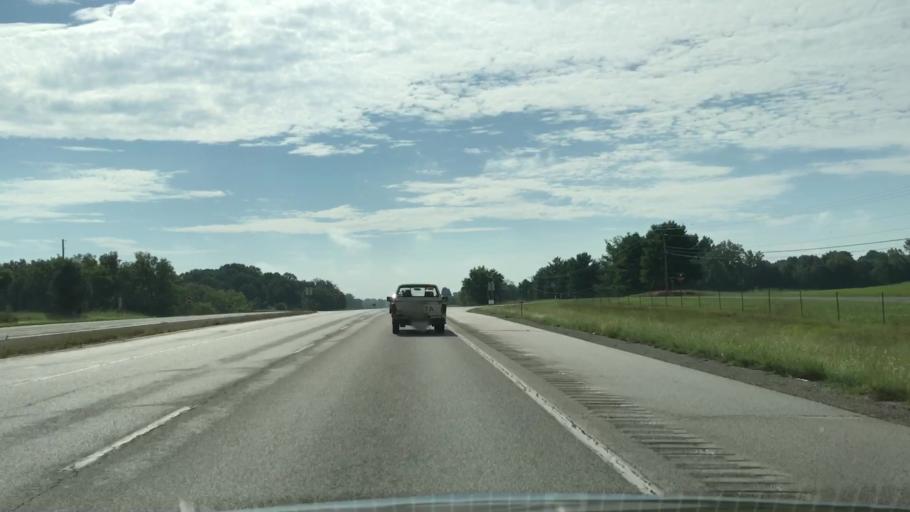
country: US
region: Kentucky
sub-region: Warren County
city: Plano
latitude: 36.8910
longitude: -86.3740
